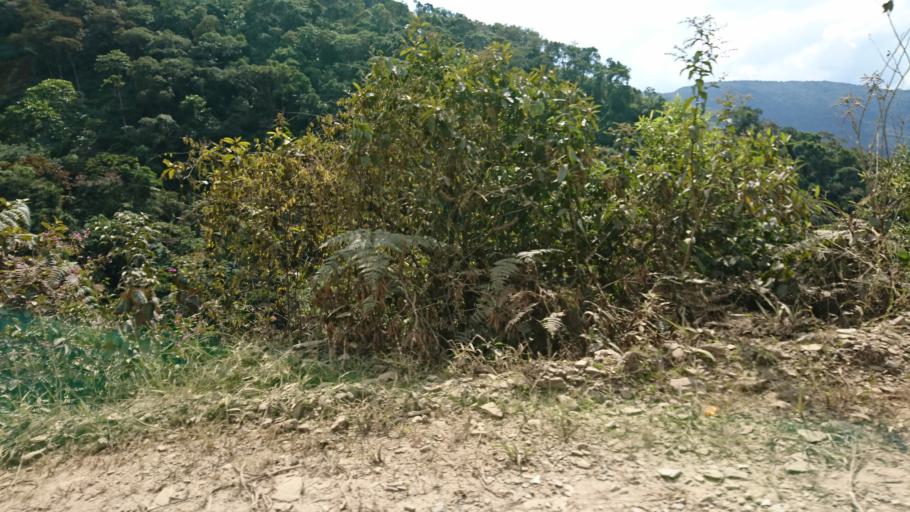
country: BO
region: La Paz
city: Coroico
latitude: -16.1278
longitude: -67.7632
